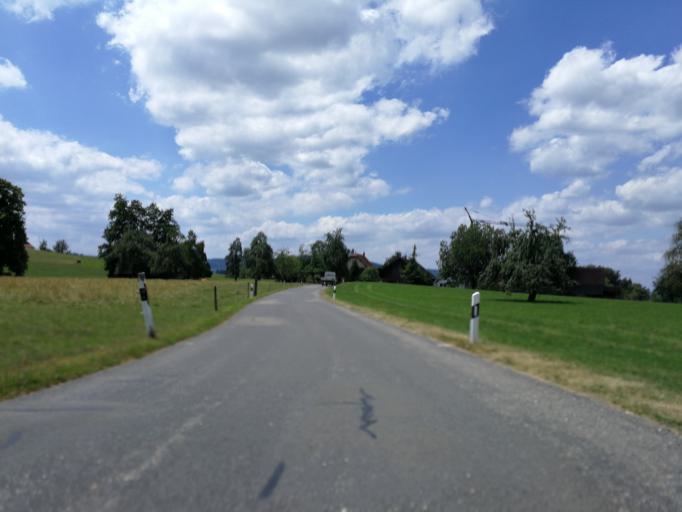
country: CH
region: Zurich
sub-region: Bezirk Hinwil
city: Gruet
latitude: 47.2884
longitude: 8.7832
